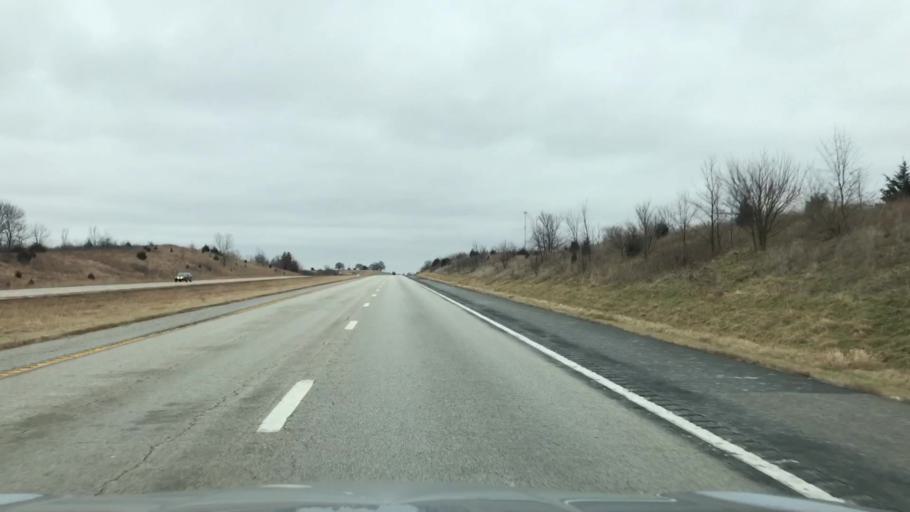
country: US
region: Missouri
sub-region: Caldwell County
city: Hamilton
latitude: 39.7491
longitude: -94.0677
